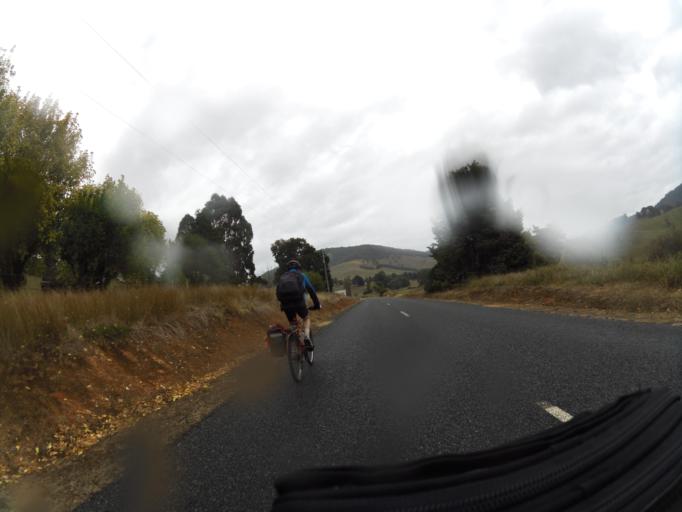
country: AU
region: New South Wales
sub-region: Greater Hume Shire
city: Holbrook
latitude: -36.2367
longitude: 147.6482
